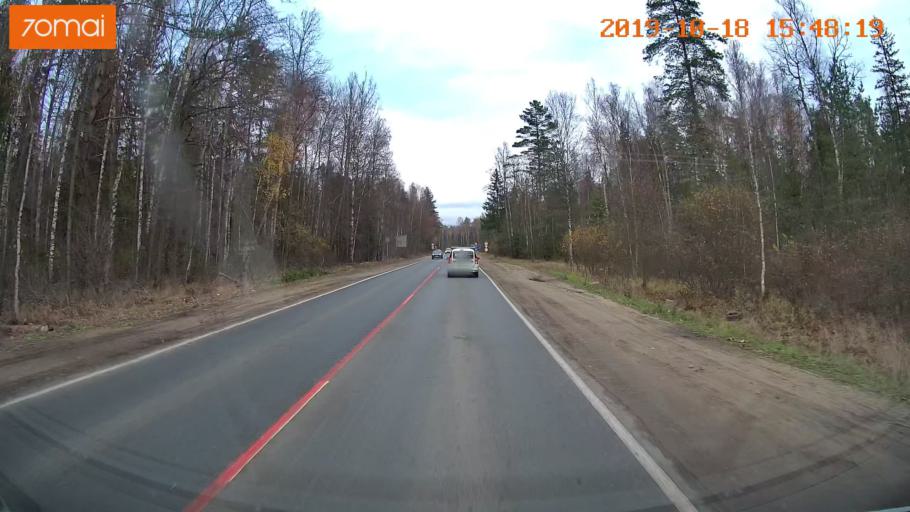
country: RU
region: Vladimir
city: Kommunar
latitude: 56.0166
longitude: 40.5788
